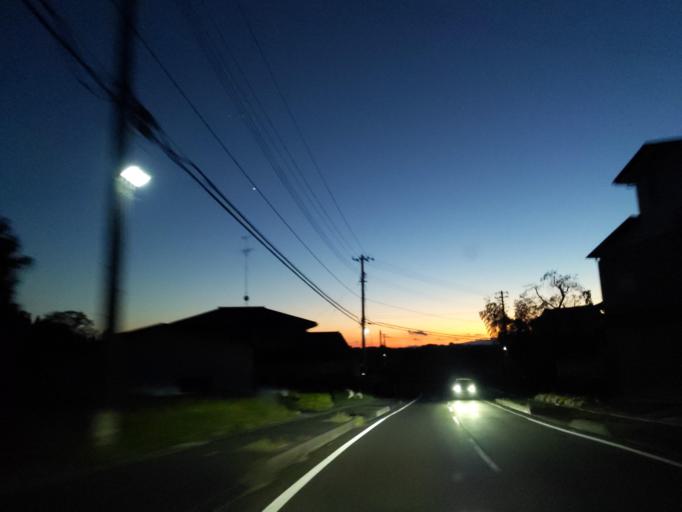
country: JP
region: Fukushima
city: Sukagawa
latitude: 37.3134
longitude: 140.3845
